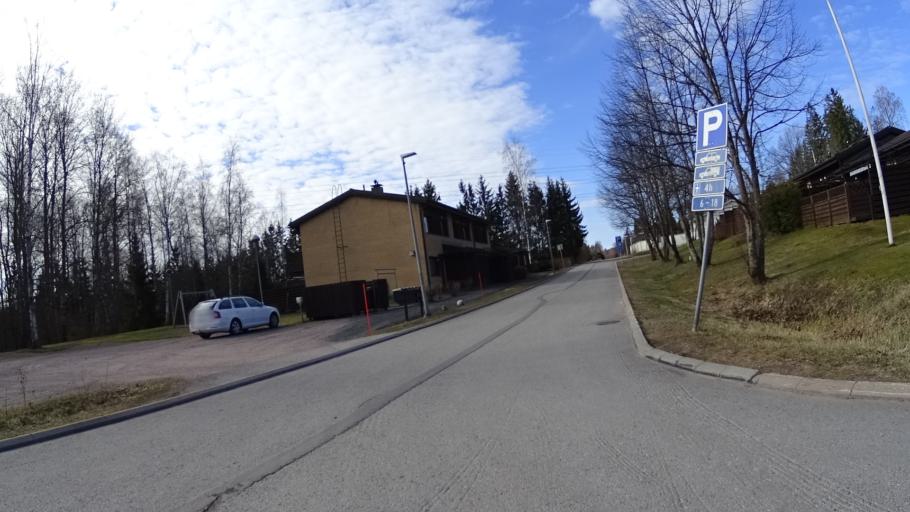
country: FI
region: Uusimaa
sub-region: Helsinki
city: Kauniainen
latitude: 60.2431
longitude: 24.7232
